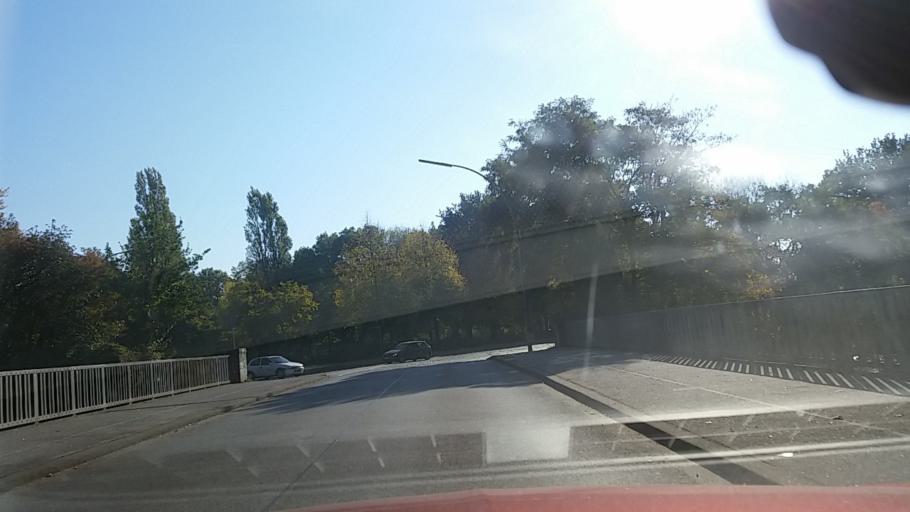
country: DE
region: Hamburg
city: Rothenburgsort
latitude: 53.5481
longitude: 10.0607
